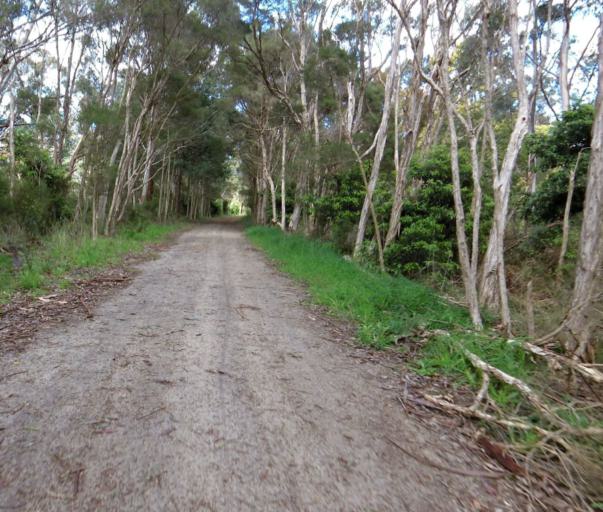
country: AU
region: Victoria
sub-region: Bass Coast
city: North Wonthaggi
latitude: -38.5394
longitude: 145.9462
